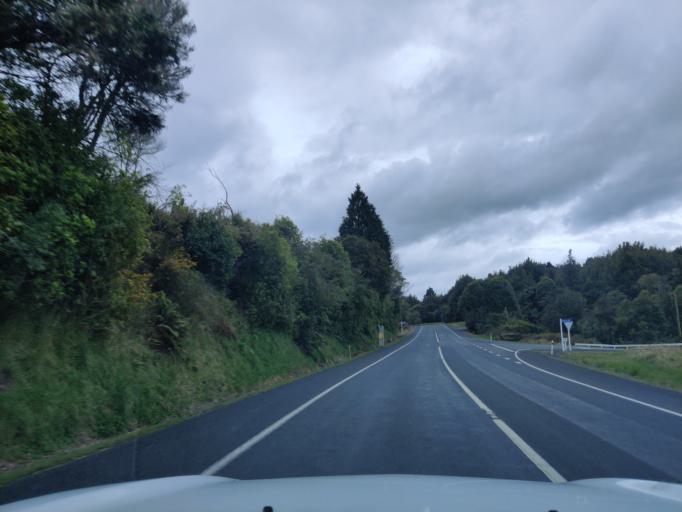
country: NZ
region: Waikato
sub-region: Otorohanga District
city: Otorohanga
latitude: -38.5061
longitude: 175.2043
